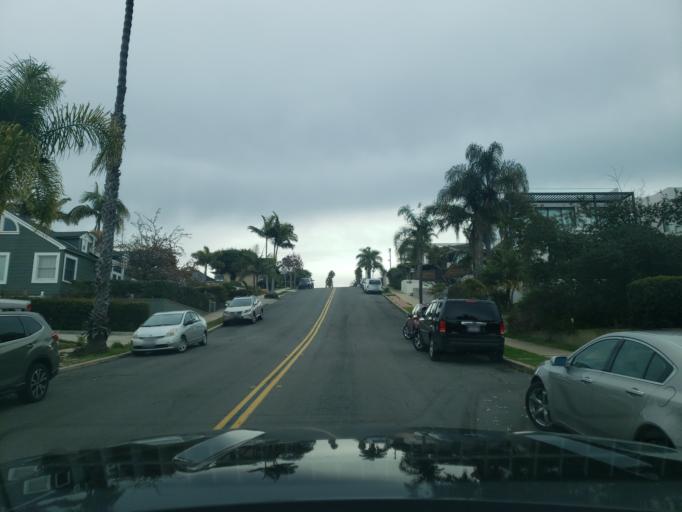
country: US
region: California
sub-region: San Diego County
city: Coronado
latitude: 32.7391
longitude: -117.2489
